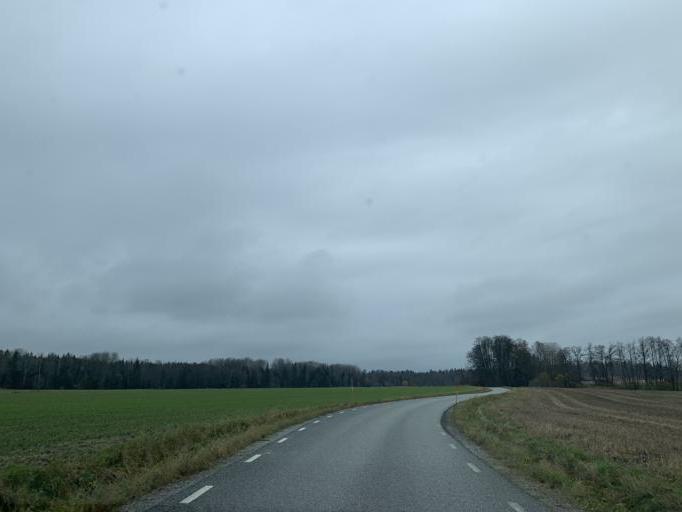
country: SE
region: Vaestmanland
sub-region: Vasteras
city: Skultuna
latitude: 59.7125
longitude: 16.4101
